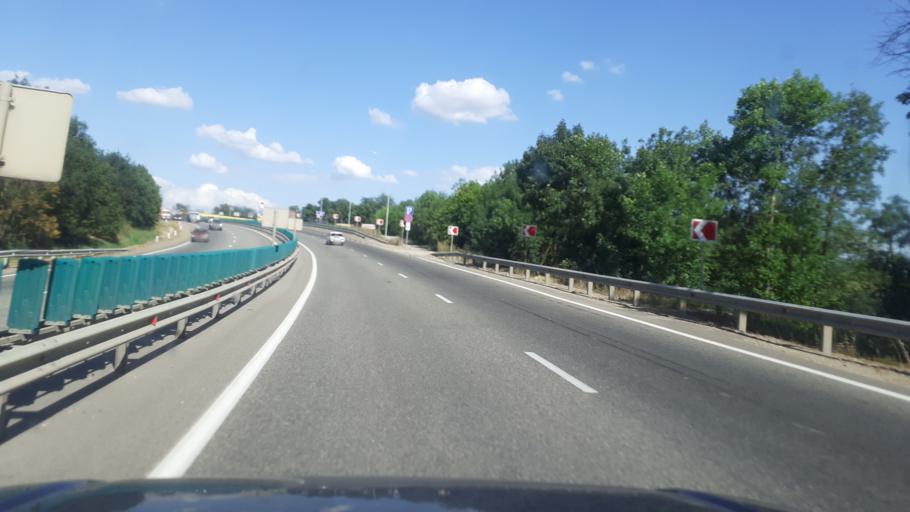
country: RU
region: Krasnodarskiy
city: Severskaya
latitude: 44.8542
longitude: 38.7392
